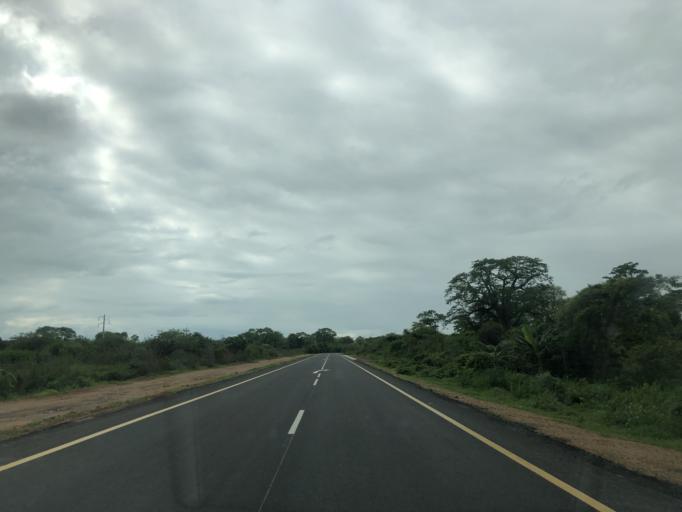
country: AO
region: Cuanza Norte
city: N'dalatando
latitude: -9.4369
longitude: 14.3116
